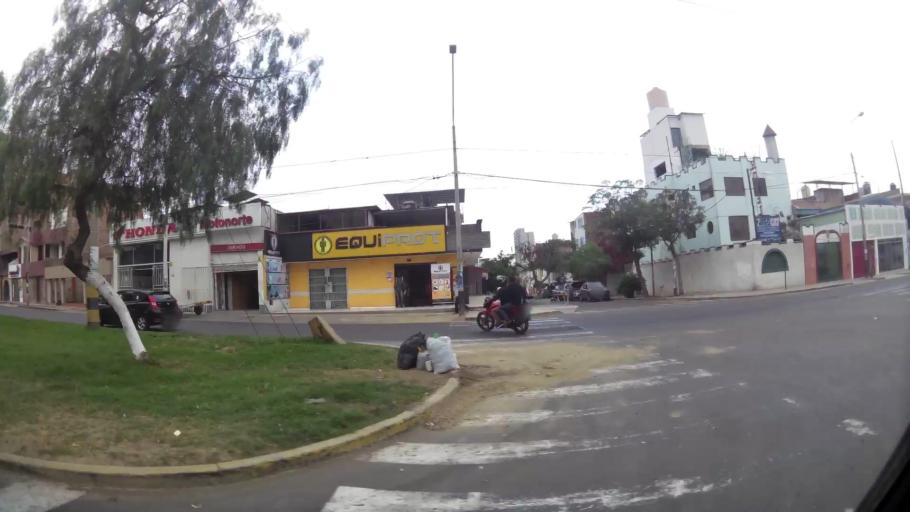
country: PE
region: La Libertad
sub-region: Provincia de Trujillo
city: Trujillo
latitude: -8.0945
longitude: -79.0268
